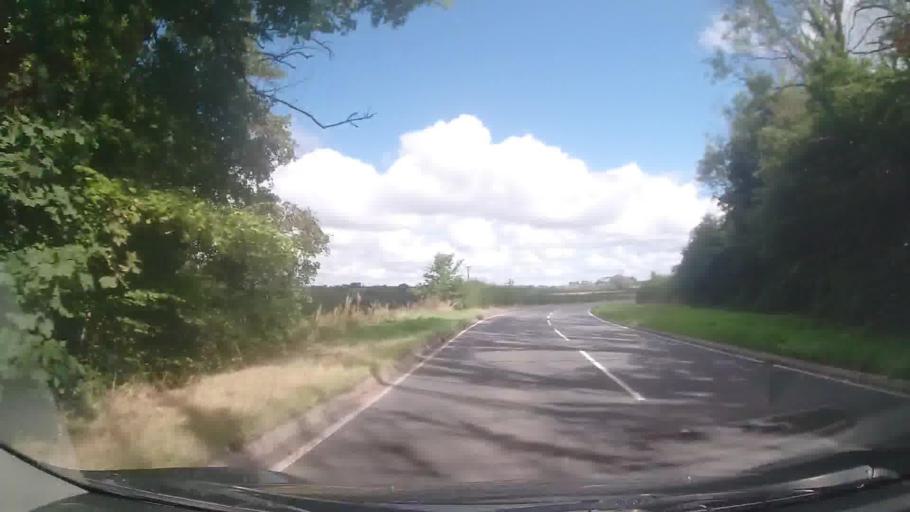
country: GB
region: Wales
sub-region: Pembrokeshire
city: Pembroke
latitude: 51.6851
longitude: -4.8795
